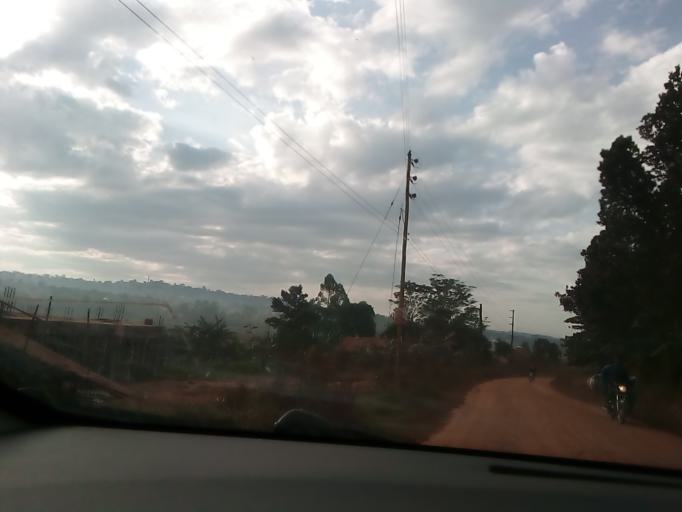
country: UG
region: Central Region
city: Masaka
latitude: -0.3529
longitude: 31.7204
